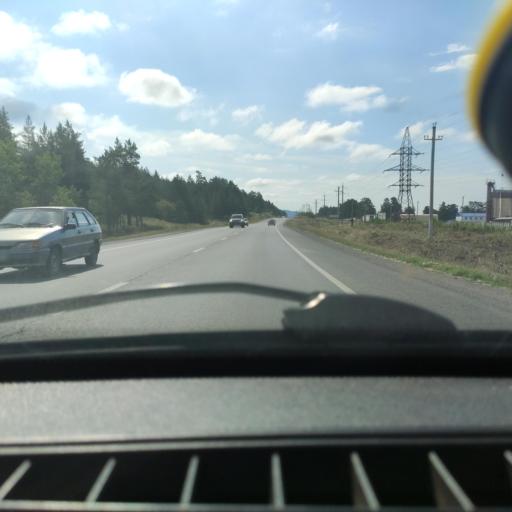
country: RU
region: Samara
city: Kurumoch
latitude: 53.4726
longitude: 50.0642
